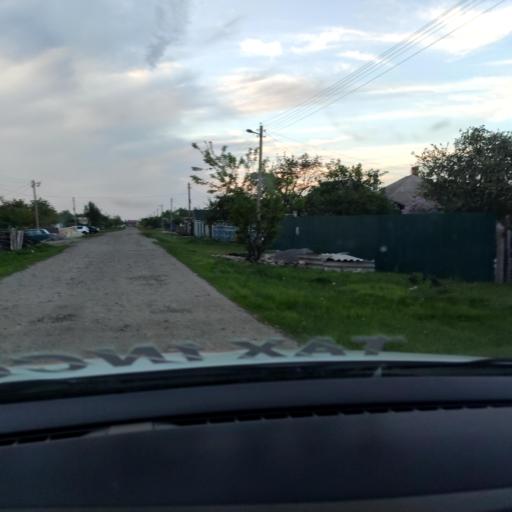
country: RU
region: Voronezj
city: Maslovka
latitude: 51.4518
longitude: 39.2371
